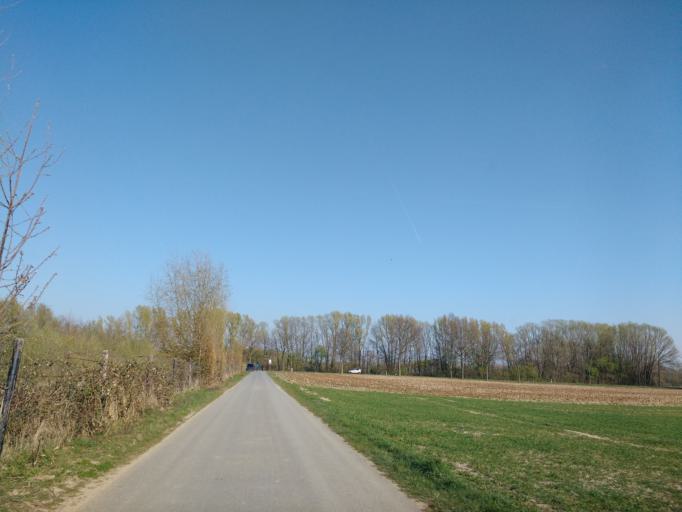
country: DE
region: North Rhine-Westphalia
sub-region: Regierungsbezirk Detmold
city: Delbruck
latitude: 51.7452
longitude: 8.6288
